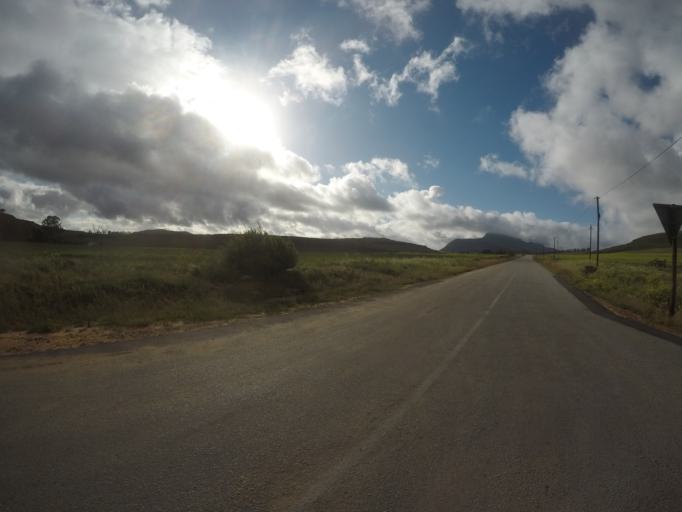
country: ZA
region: Western Cape
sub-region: West Coast District Municipality
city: Clanwilliam
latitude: -32.3423
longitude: 18.8371
